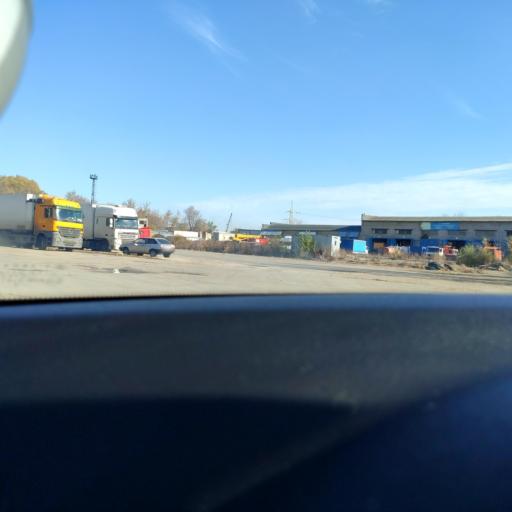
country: RU
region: Samara
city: Petra-Dubrava
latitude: 53.2589
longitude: 50.2991
